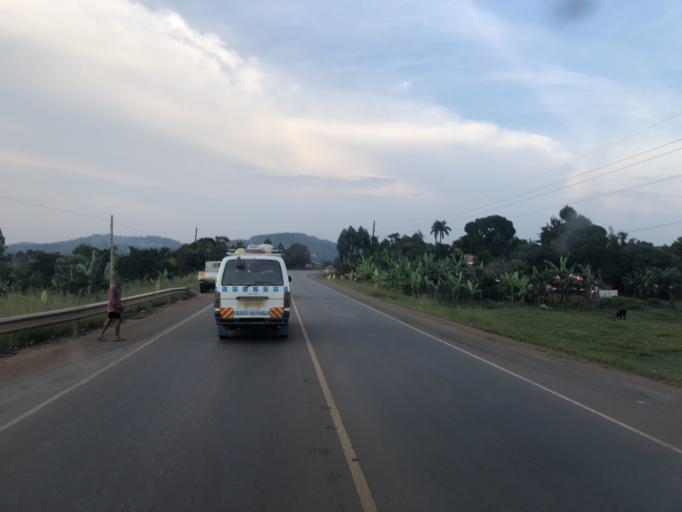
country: UG
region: Central Region
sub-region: Mpigi District
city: Mpigi
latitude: 0.2375
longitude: 32.3483
